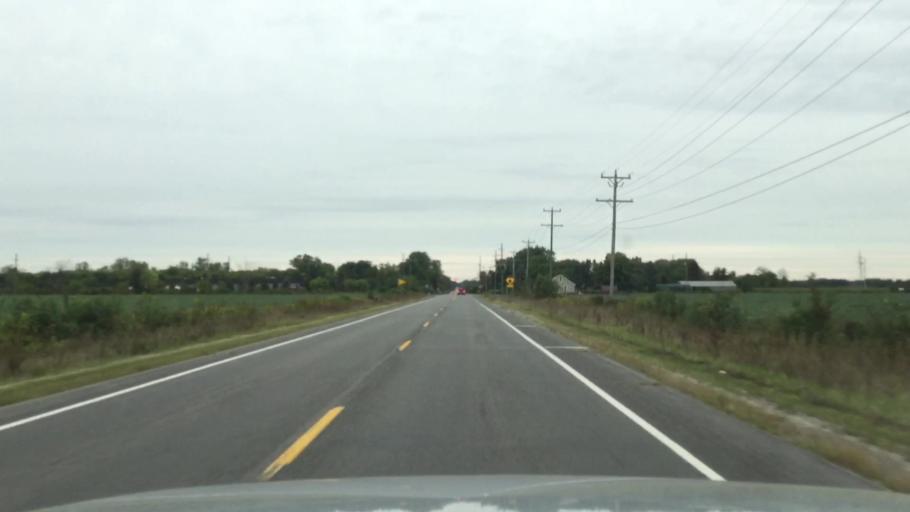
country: US
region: Michigan
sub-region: Washtenaw County
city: Milan
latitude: 42.1106
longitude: -83.6770
